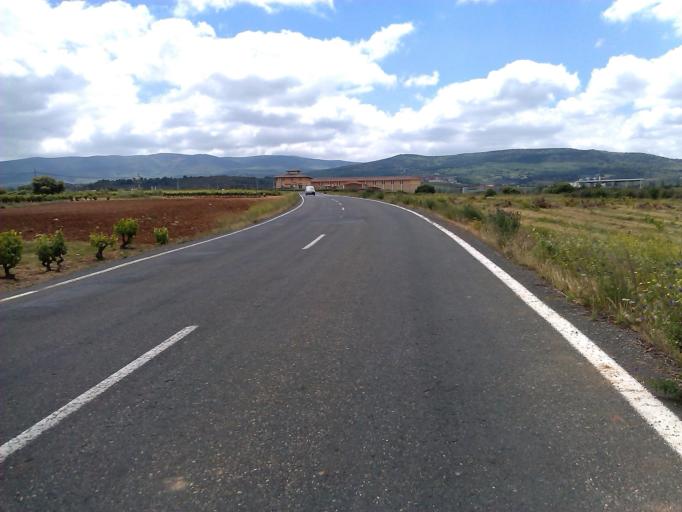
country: ES
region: La Rioja
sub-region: Provincia de La Rioja
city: Hornos de Moncalvillo
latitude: 42.4178
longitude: -2.5917
